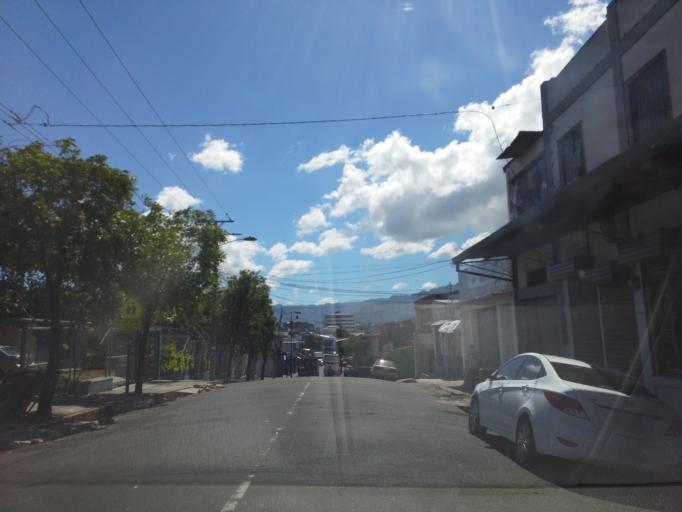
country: CR
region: San Jose
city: San Jose
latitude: 9.9414
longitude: -84.0851
